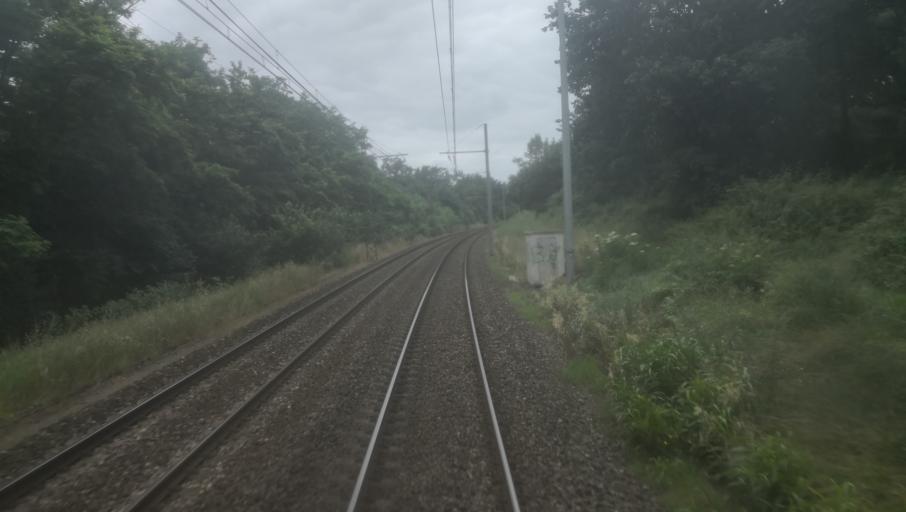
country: FR
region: Midi-Pyrenees
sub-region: Departement du Tarn-et-Garonne
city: Verdun-sur-Garonne
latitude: 43.8715
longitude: 1.2713
